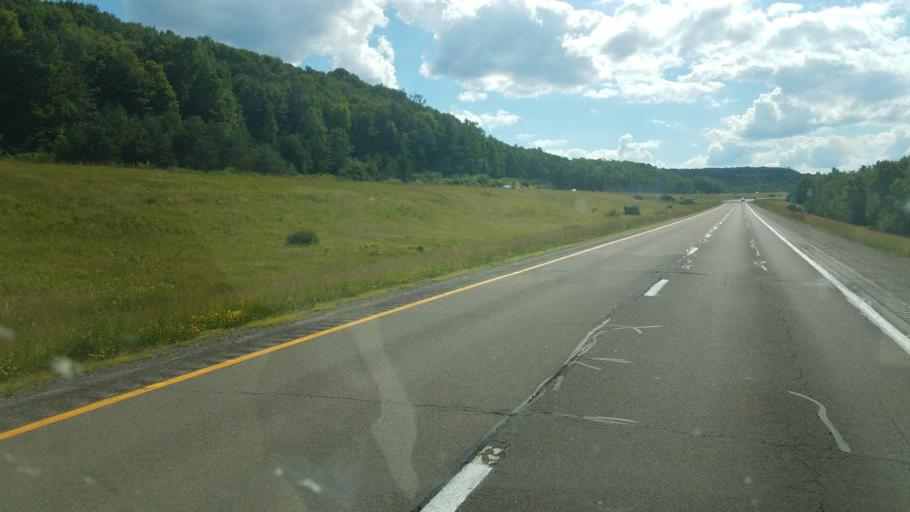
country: US
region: New York
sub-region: Allegany County
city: Alfred
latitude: 42.3181
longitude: -77.8100
